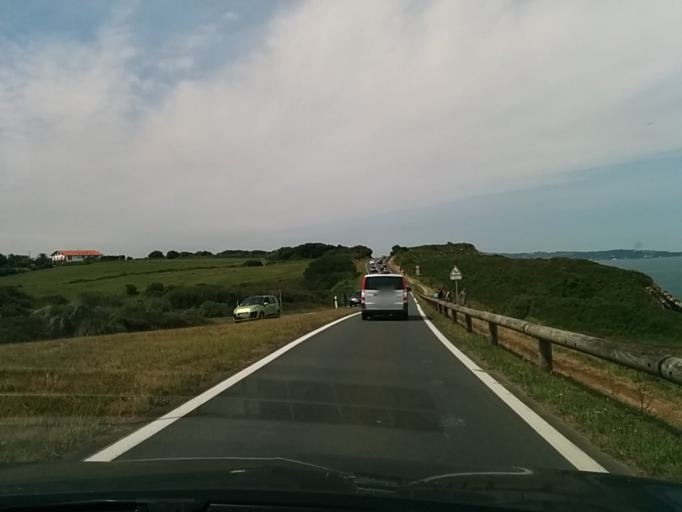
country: FR
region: Aquitaine
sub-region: Departement des Pyrenees-Atlantiques
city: Ciboure
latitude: 43.3908
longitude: -1.7017
